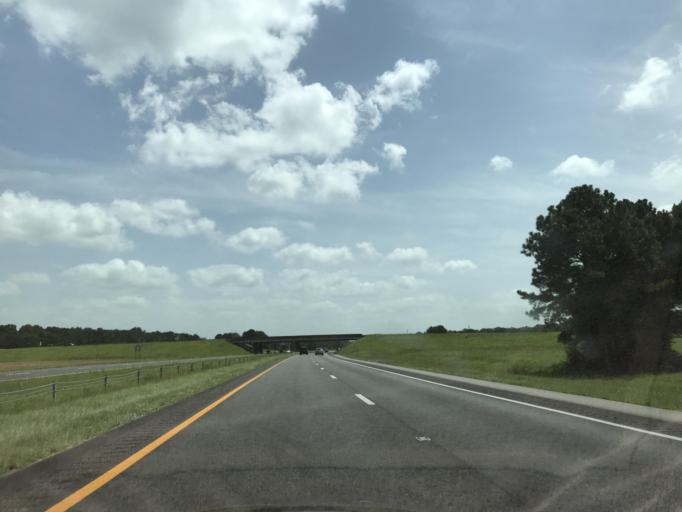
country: US
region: North Carolina
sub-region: Wayne County
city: Mount Olive
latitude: 35.1186
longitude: -78.1884
